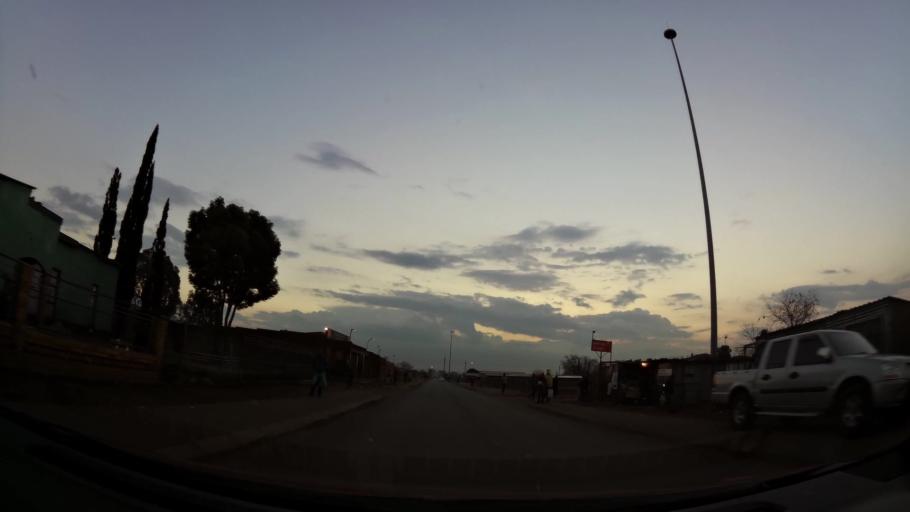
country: ZA
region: Gauteng
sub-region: City of Johannesburg Metropolitan Municipality
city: Orange Farm
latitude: -26.5540
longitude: 27.8509
